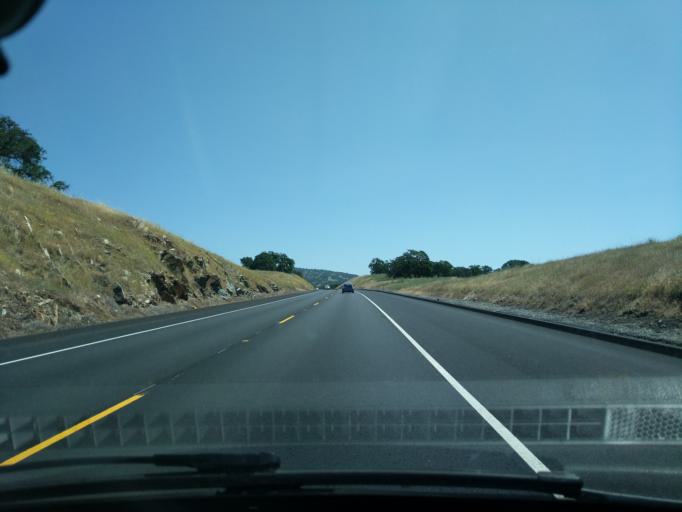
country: US
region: California
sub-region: Calaveras County
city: Copperopolis
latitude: 37.9412
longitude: -120.7421
